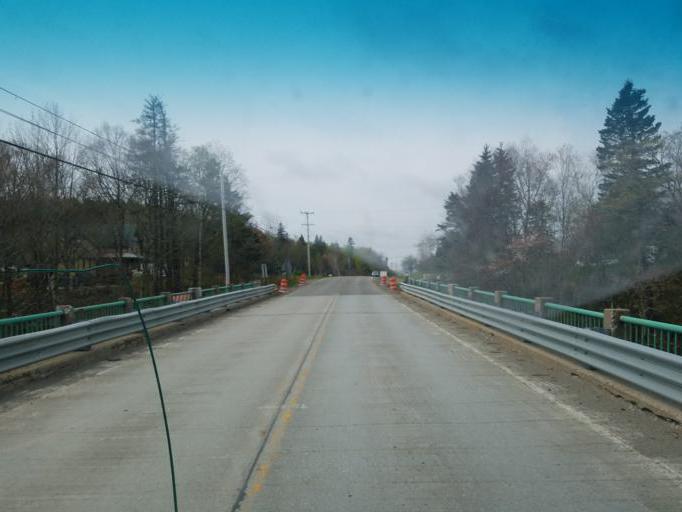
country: US
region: Maine
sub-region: Washington County
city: East Machias
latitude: 44.7844
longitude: -67.1895
